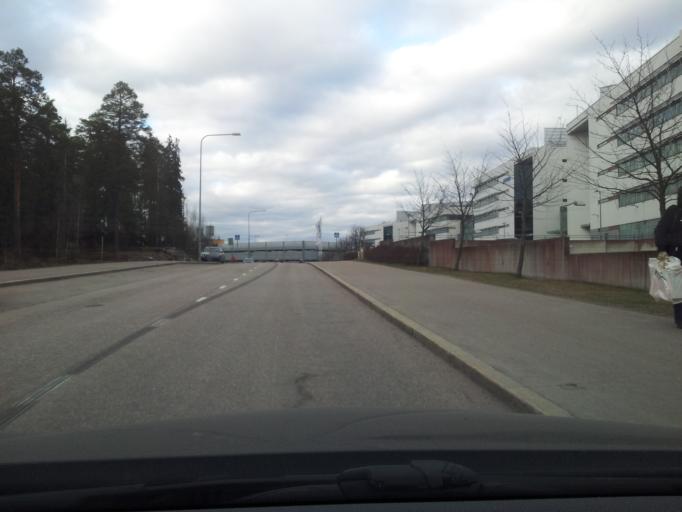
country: FI
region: Uusimaa
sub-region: Helsinki
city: Otaniemi
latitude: 60.2100
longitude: 24.8121
